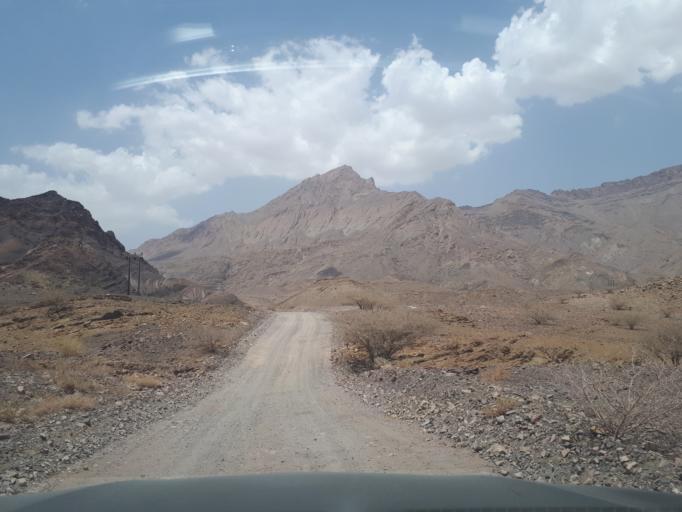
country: OM
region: Ash Sharqiyah
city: Badiyah
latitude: 22.4996
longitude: 59.1189
